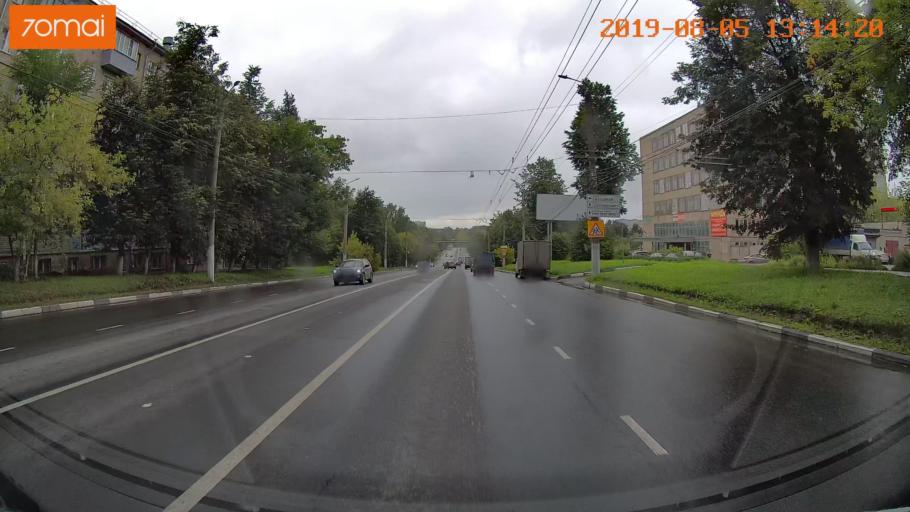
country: RU
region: Ivanovo
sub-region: Gorod Ivanovo
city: Ivanovo
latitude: 56.9942
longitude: 41.0085
